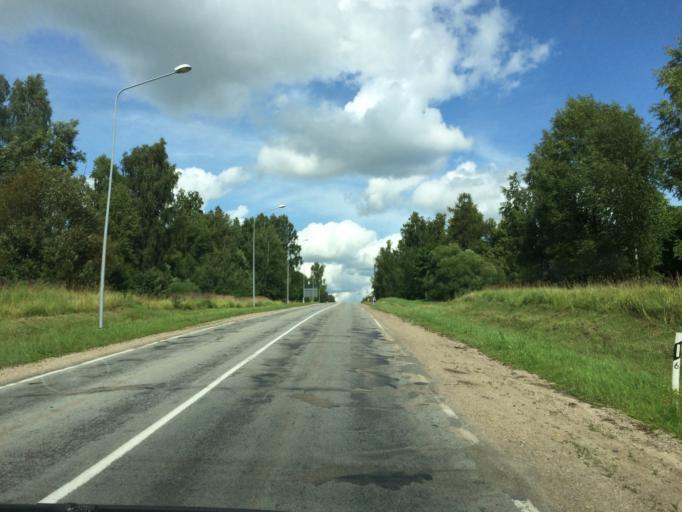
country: LV
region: Rezekne
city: Rezekne
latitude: 56.5461
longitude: 27.3550
